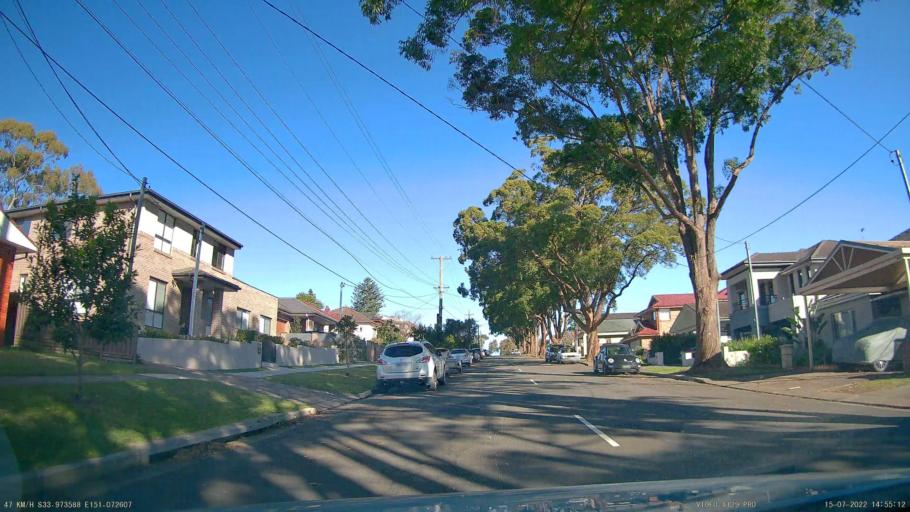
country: AU
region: New South Wales
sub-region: Hurstville
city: Oatley
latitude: -33.9738
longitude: 151.0726
